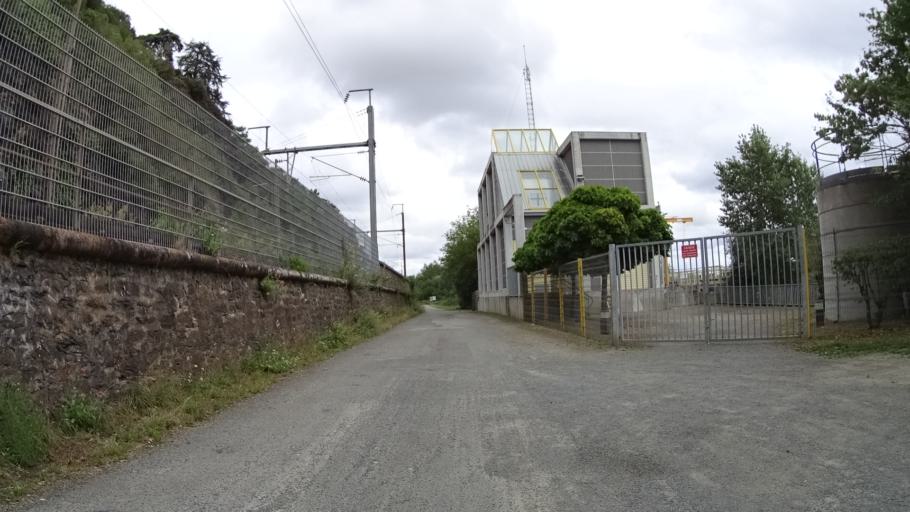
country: FR
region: Pays de la Loire
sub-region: Departement de la Loire-Atlantique
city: Mauves-sur-Loire
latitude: 47.2955
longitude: -1.3797
